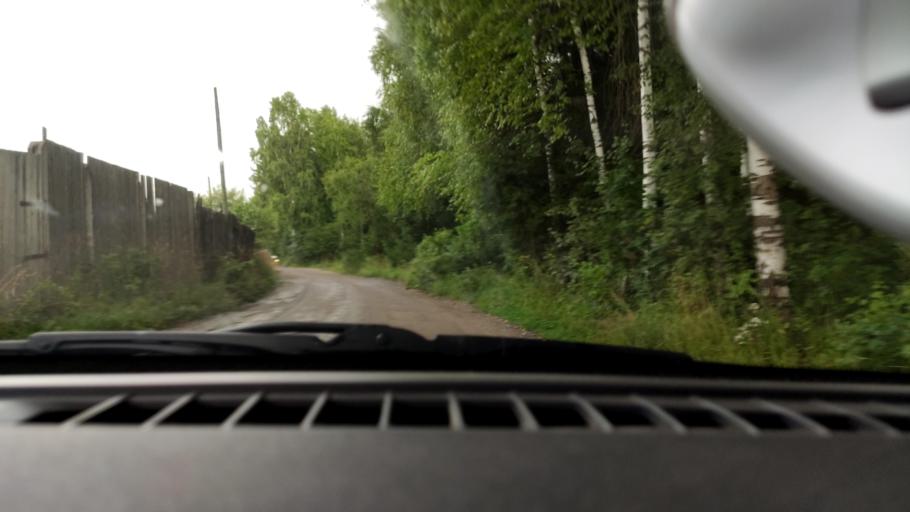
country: RU
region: Perm
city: Overyata
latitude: 58.0523
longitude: 55.9863
